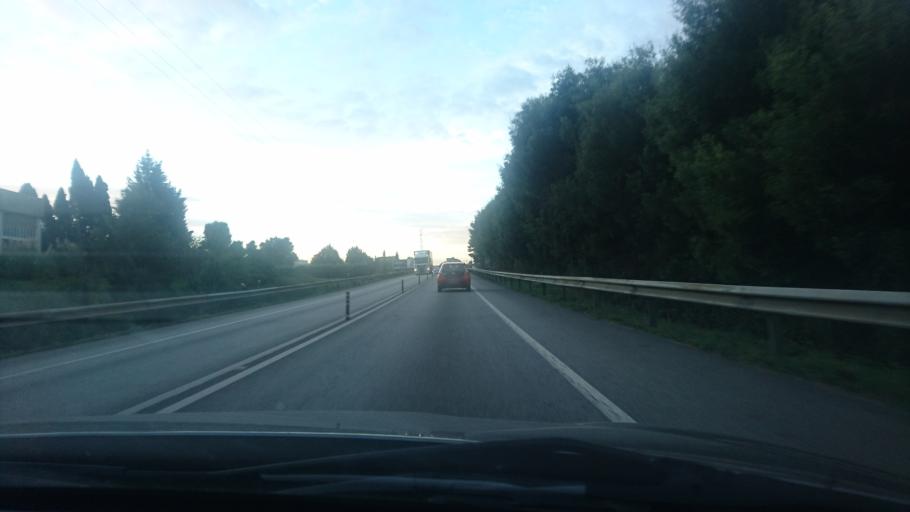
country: PT
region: Aveiro
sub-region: Sao Joao da Madeira
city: Sao Joao da Madeira
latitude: 40.8996
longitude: -8.4823
